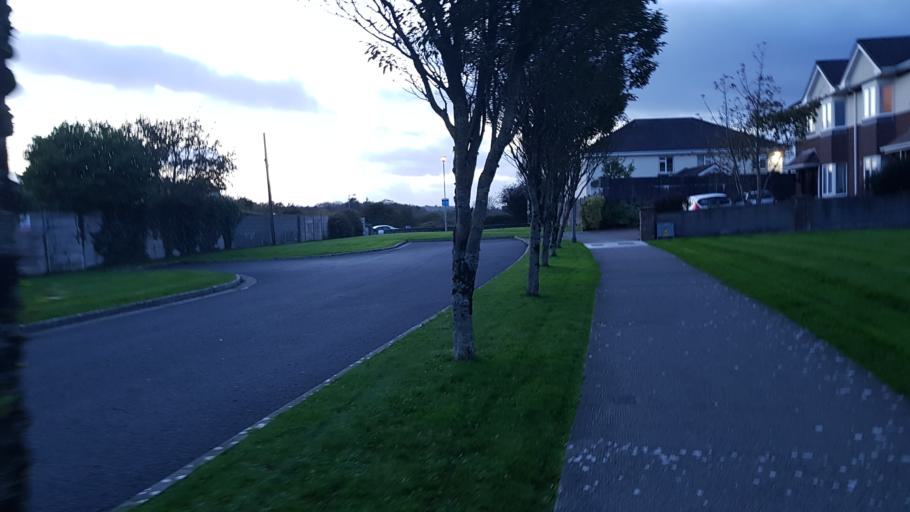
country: IE
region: Connaught
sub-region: County Galway
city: Gaillimh
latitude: 53.2838
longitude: -9.0565
